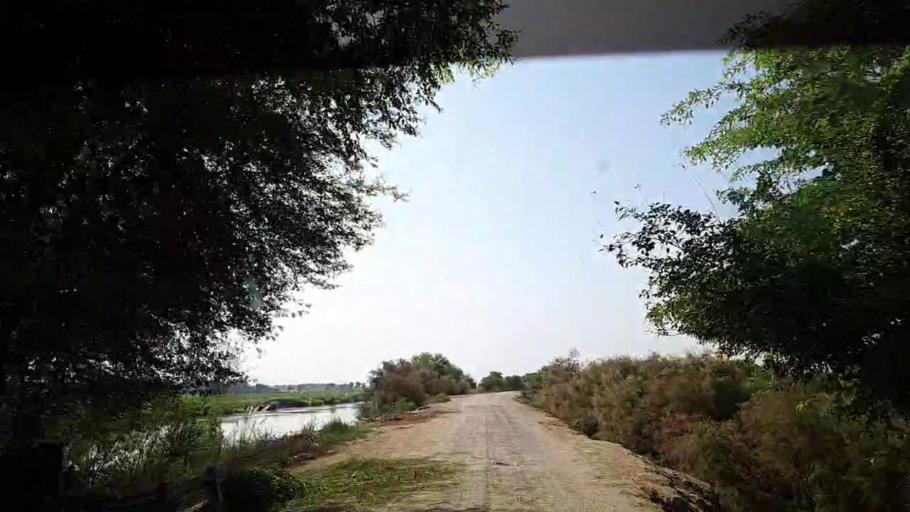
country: PK
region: Sindh
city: Ghauspur
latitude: 28.1888
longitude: 69.0615
